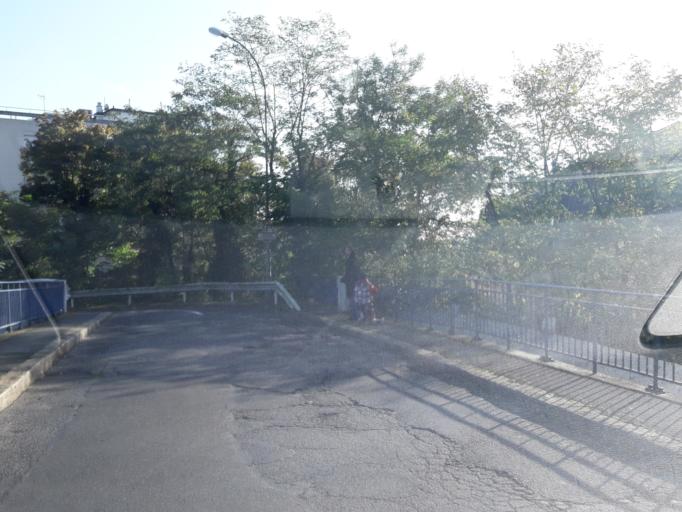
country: FR
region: Ile-de-France
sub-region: Departement du Val-de-Marne
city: Ablon-sur-Seine
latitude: 48.7209
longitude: 2.4155
